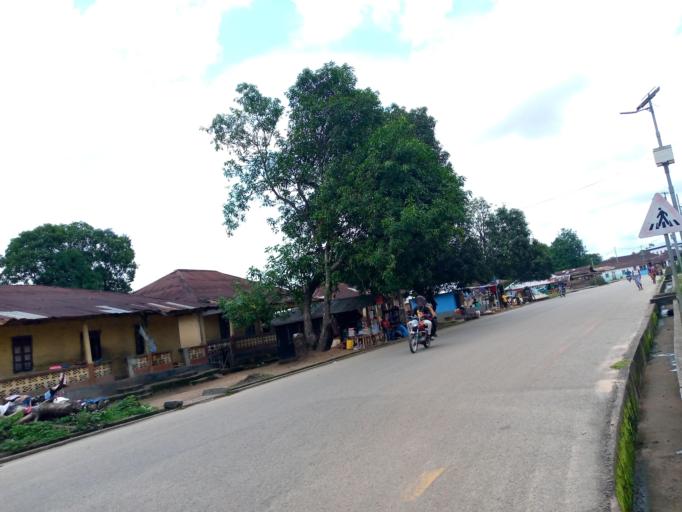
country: SL
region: Northern Province
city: Magburaka
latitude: 8.7212
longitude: -11.9560
